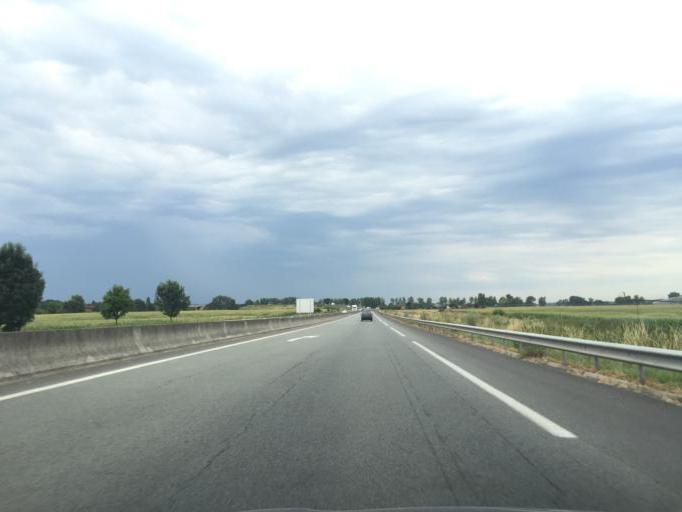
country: FR
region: Auvergne
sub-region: Departement de l'Allier
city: Toulon-sur-Allier
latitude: 46.5086
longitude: 3.3567
